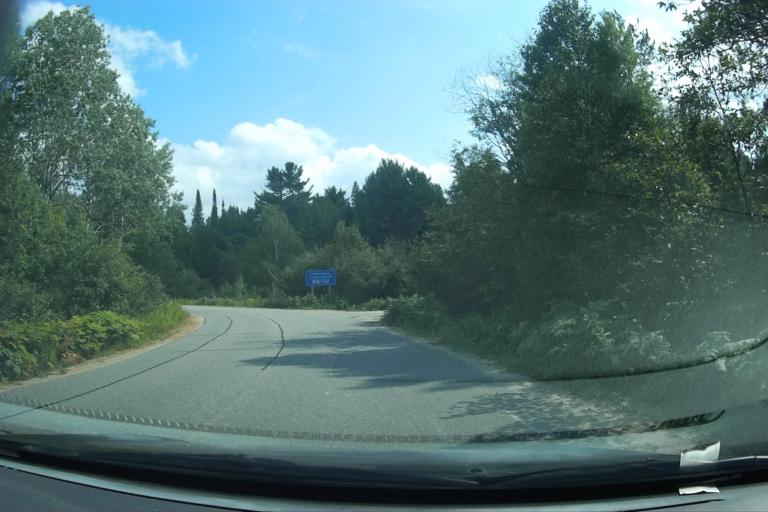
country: CA
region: Ontario
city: Bancroft
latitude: 45.5876
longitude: -78.3673
